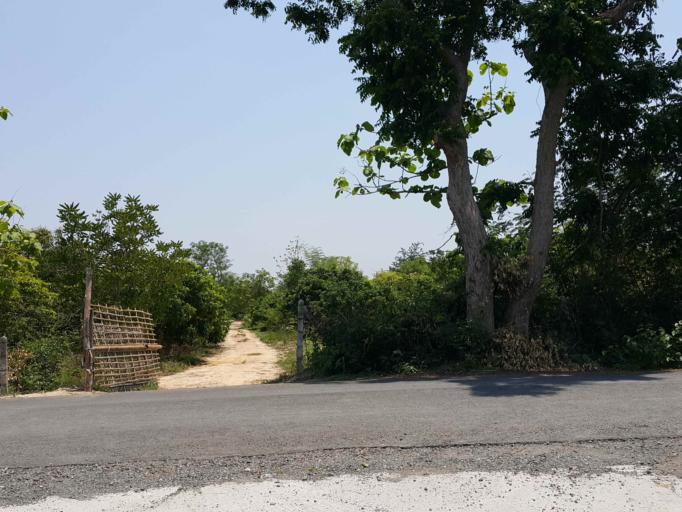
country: TH
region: Chiang Mai
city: San Sai
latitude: 18.8345
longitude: 99.1051
